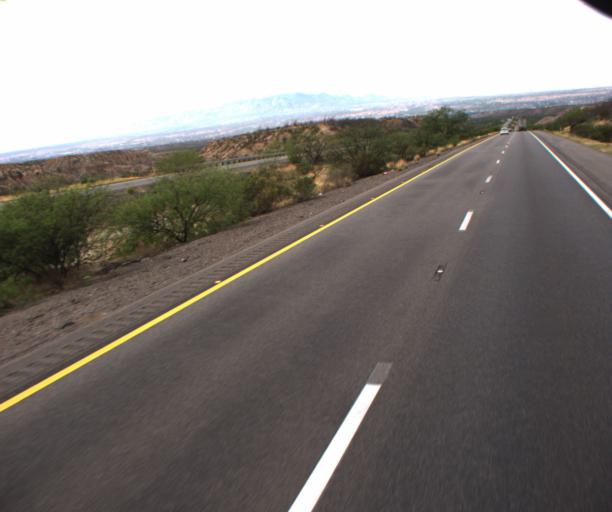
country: US
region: Arizona
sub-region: Cochise County
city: Saint David
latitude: 31.9832
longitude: -110.2063
